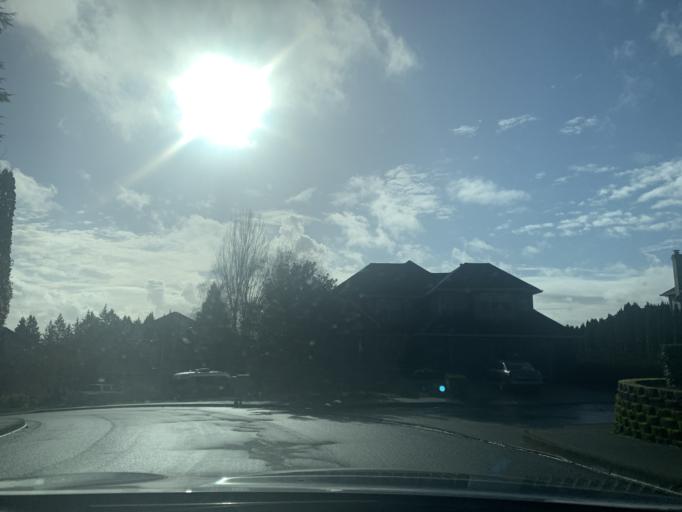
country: US
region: Oregon
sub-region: Washington County
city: King City
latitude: 45.4037
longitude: -122.8279
